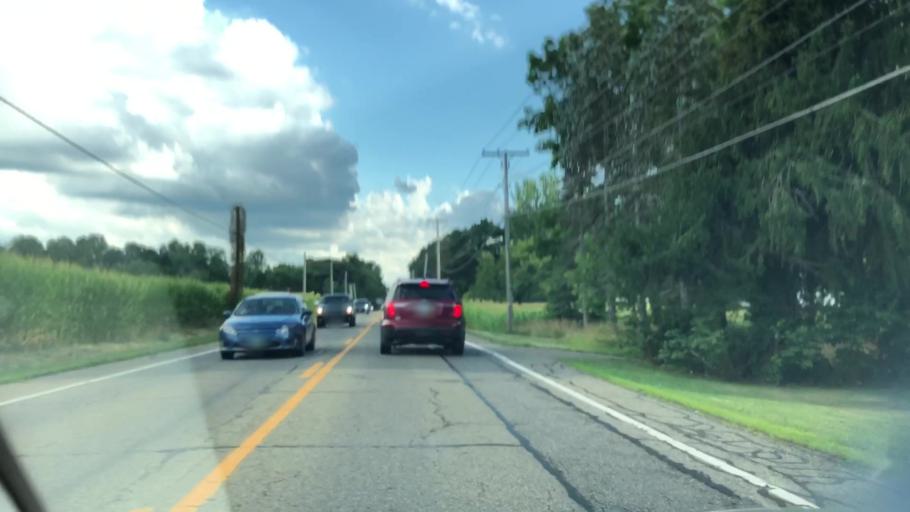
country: US
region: Ohio
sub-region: Summit County
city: Green
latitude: 40.9625
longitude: -81.4940
